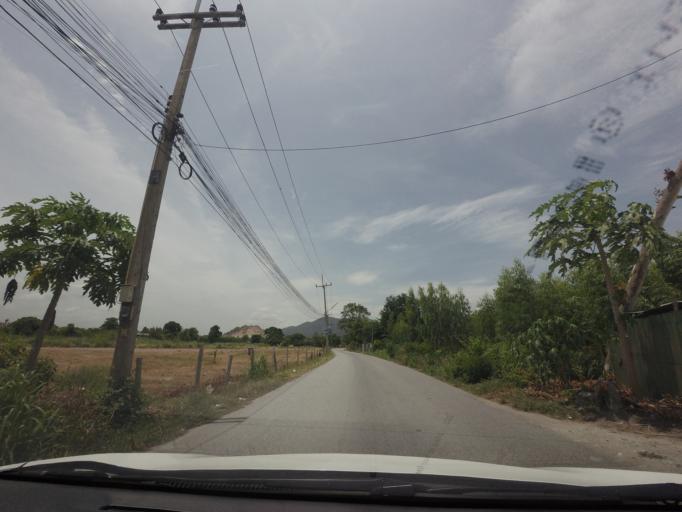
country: TH
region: Chon Buri
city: Chon Buri
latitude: 13.2926
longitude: 100.9743
